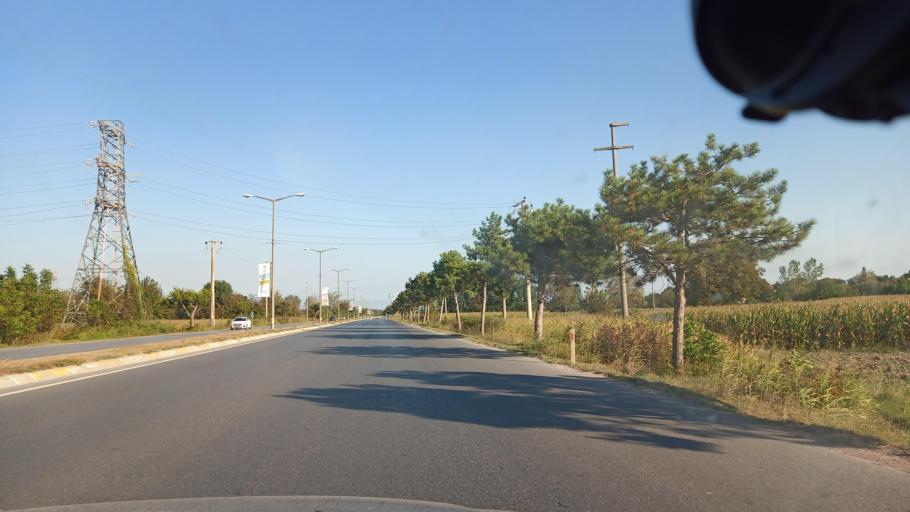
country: TR
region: Sakarya
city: Kazimpasa
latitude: 40.8427
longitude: 30.3352
